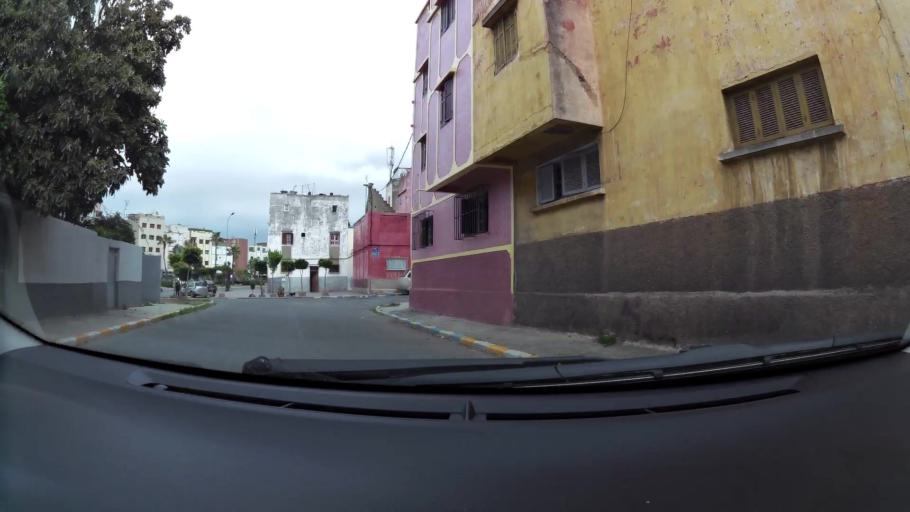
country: MA
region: Grand Casablanca
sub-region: Casablanca
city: Casablanca
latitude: 33.5665
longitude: -7.5582
